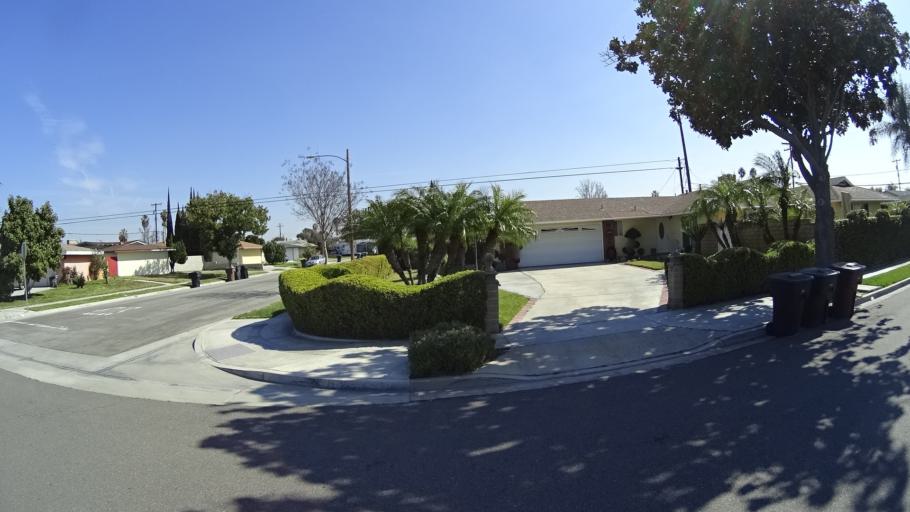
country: US
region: California
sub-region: Orange County
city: Buena Park
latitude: 33.8510
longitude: -117.9645
